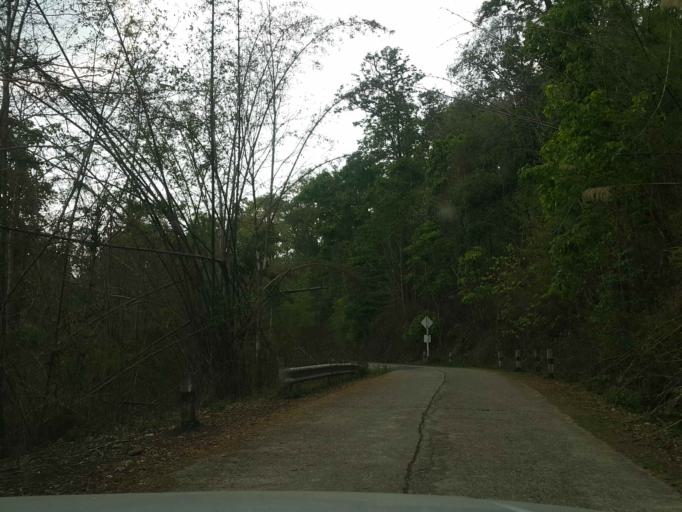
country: TH
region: Chiang Mai
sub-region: Amphoe Chiang Dao
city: Chiang Dao
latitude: 19.3845
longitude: 98.7753
